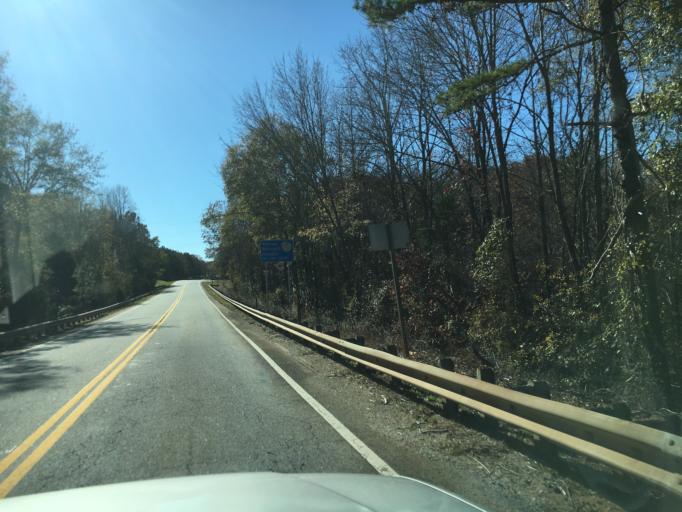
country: US
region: Georgia
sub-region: Hart County
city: Hartwell
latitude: 34.3523
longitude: -82.8169
